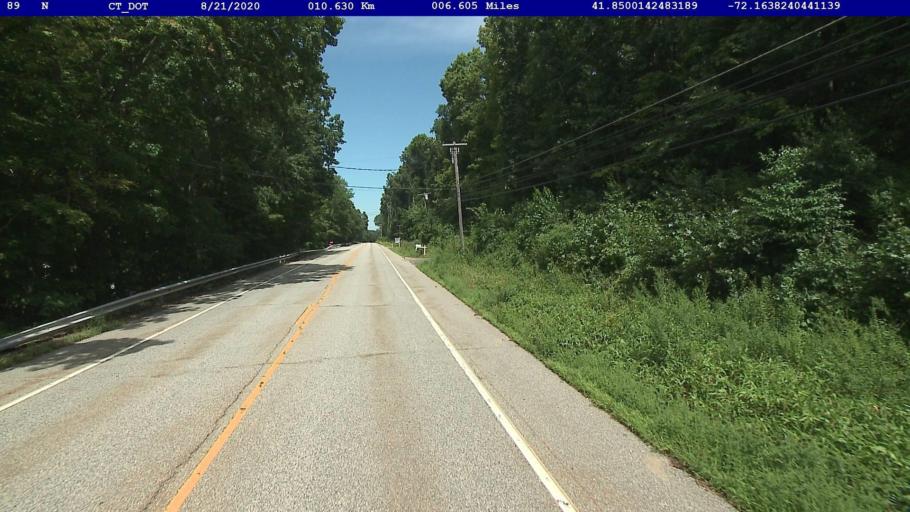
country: US
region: Connecticut
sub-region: Tolland County
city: Storrs
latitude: 41.8499
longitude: -72.1638
